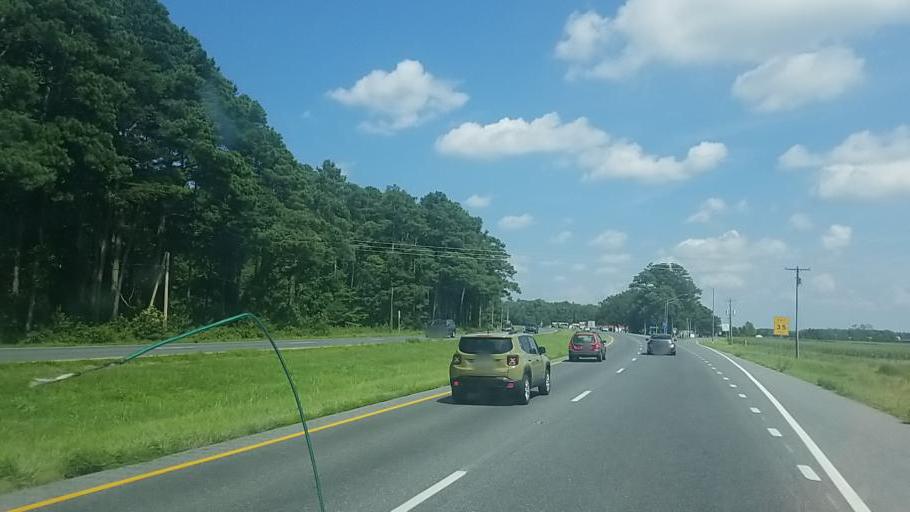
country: US
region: Maryland
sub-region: Wicomico County
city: Hebron
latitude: 38.4614
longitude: -75.7797
